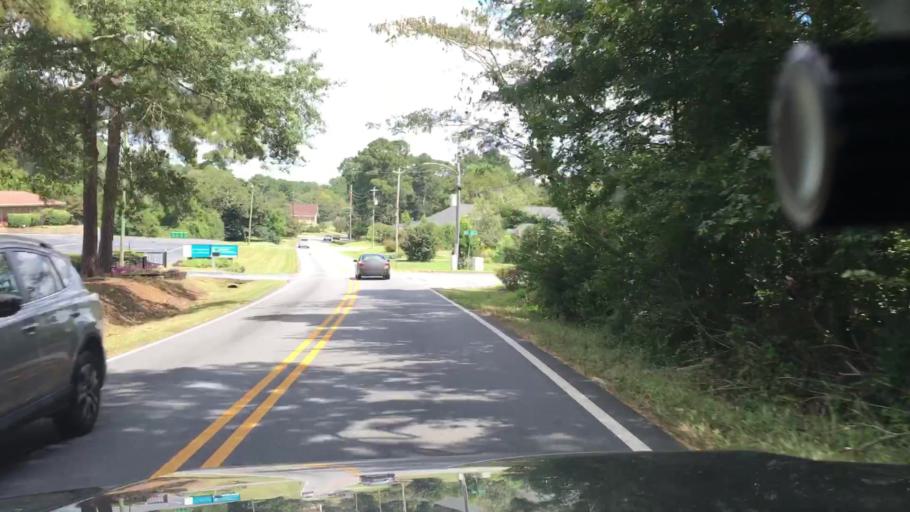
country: US
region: Georgia
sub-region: Bibb County
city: Macon
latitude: 32.8757
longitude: -83.6876
